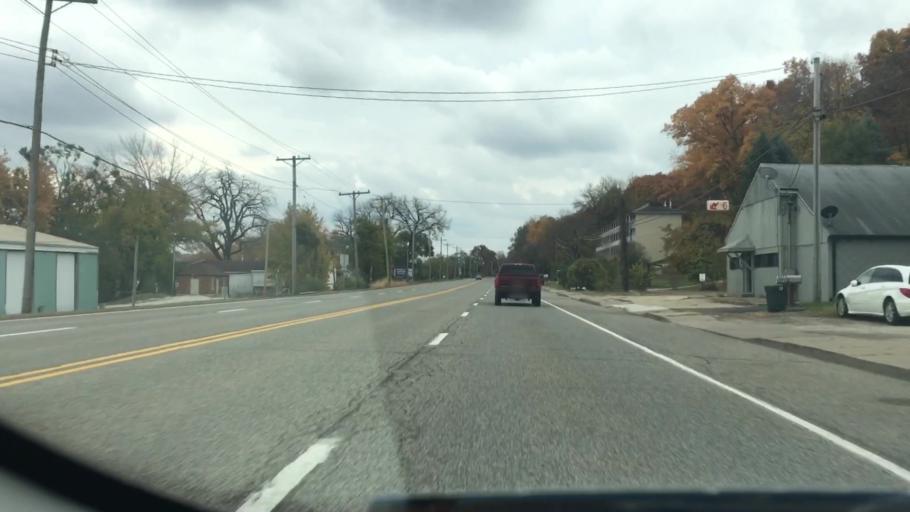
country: US
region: Illinois
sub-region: Peoria County
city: Peoria Heights
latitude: 40.7462
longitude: -89.5570
